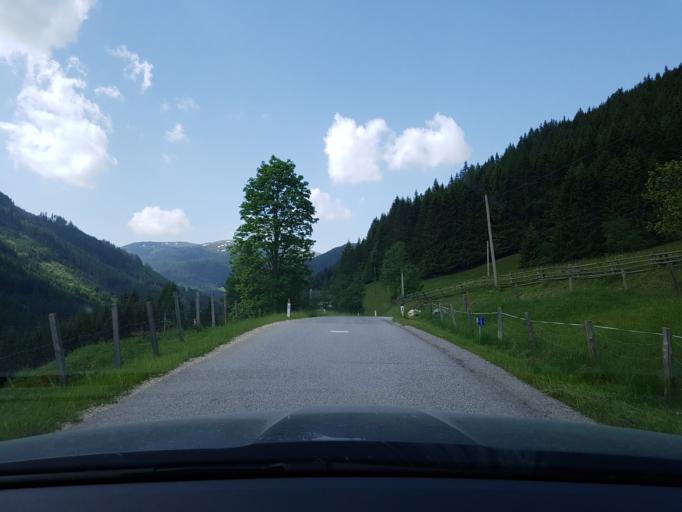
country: AT
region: Salzburg
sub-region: Politischer Bezirk Tamsweg
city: Thomatal
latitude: 47.0640
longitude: 13.7183
